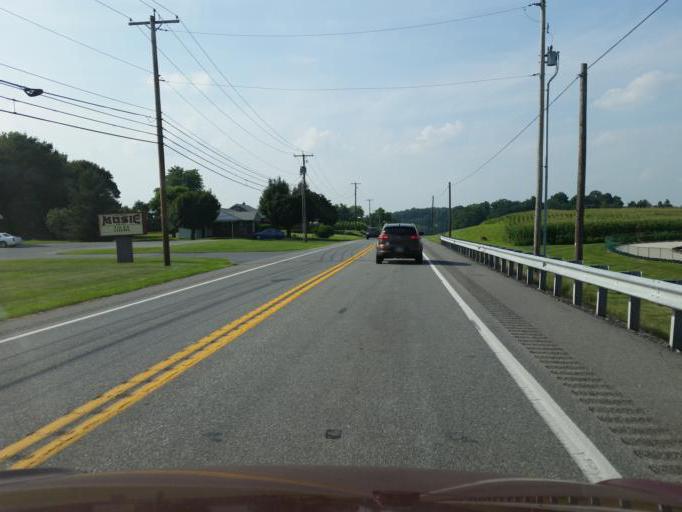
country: US
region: Pennsylvania
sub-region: Dauphin County
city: Hershey
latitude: 40.2361
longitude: -76.6238
